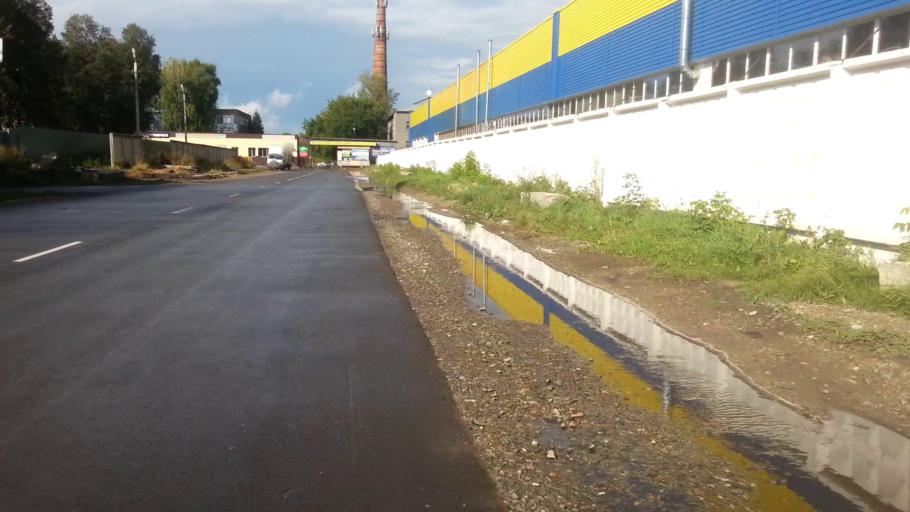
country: RU
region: Altai Krai
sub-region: Gorod Barnaulskiy
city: Barnaul
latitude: 53.3431
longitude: 83.7229
